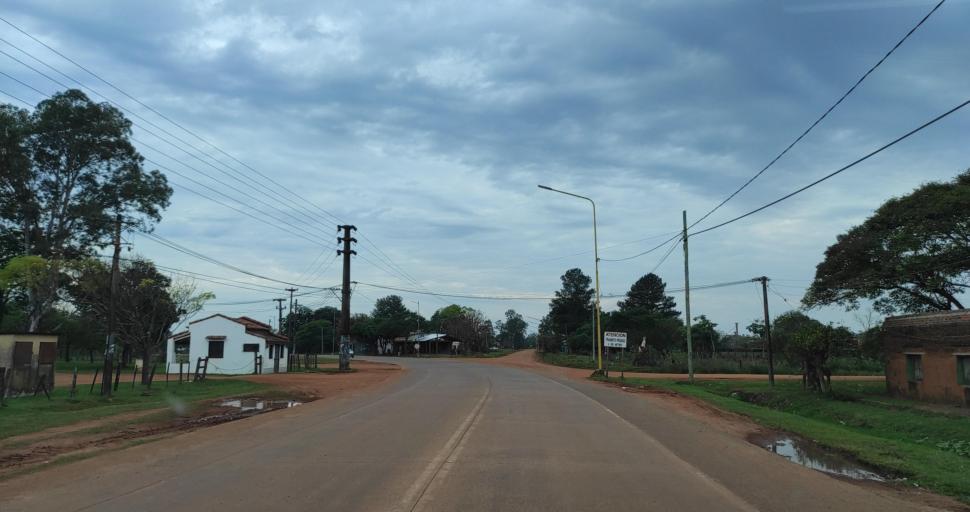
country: AR
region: Corrientes
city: Santo Tome
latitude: -28.5509
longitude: -56.0675
